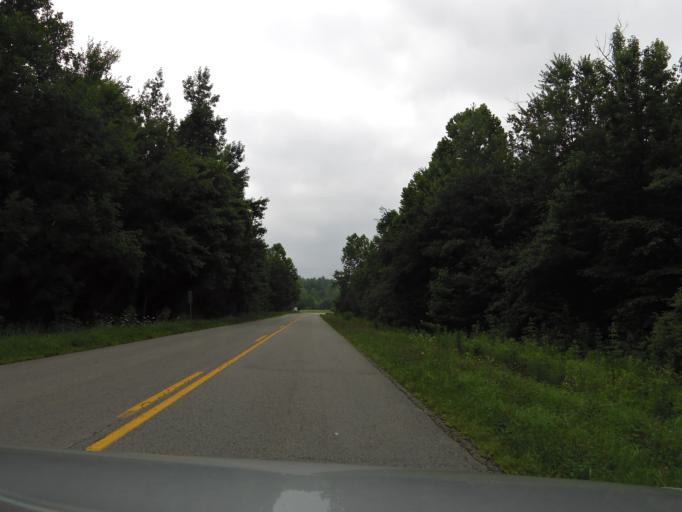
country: US
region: Kentucky
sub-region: Muhlenberg County
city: Morehead
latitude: 37.2933
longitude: -87.3101
